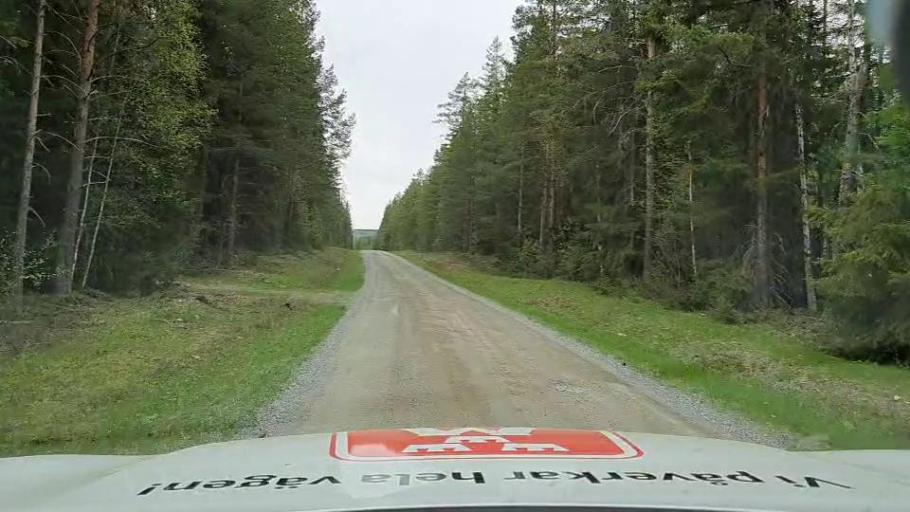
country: SE
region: Jaemtland
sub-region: Bergs Kommun
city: Hoverberg
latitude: 62.4983
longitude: 14.7070
